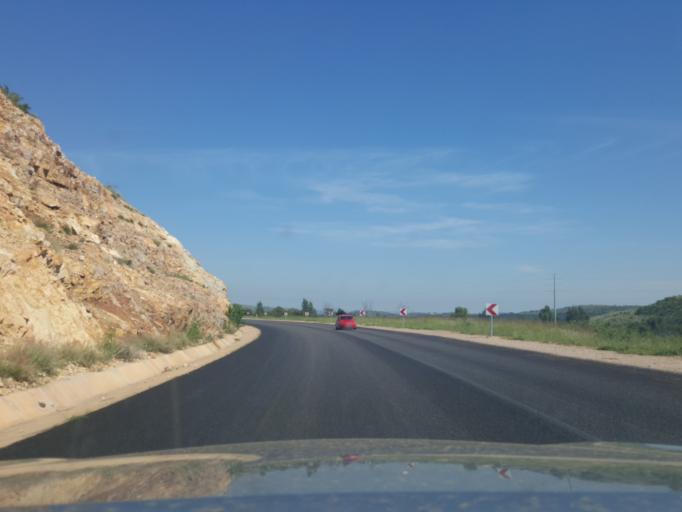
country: ZA
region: Gauteng
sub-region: City of Tshwane Metropolitan Municipality
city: Cullinan
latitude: -25.6786
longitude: 28.5062
